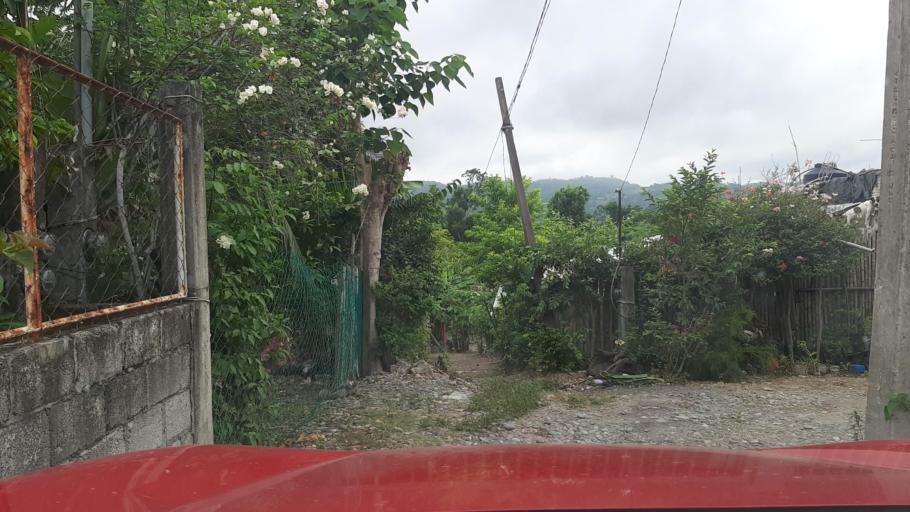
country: MX
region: Veracruz
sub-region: Papantla
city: Residencial Tajin
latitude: 20.6064
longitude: -97.4293
